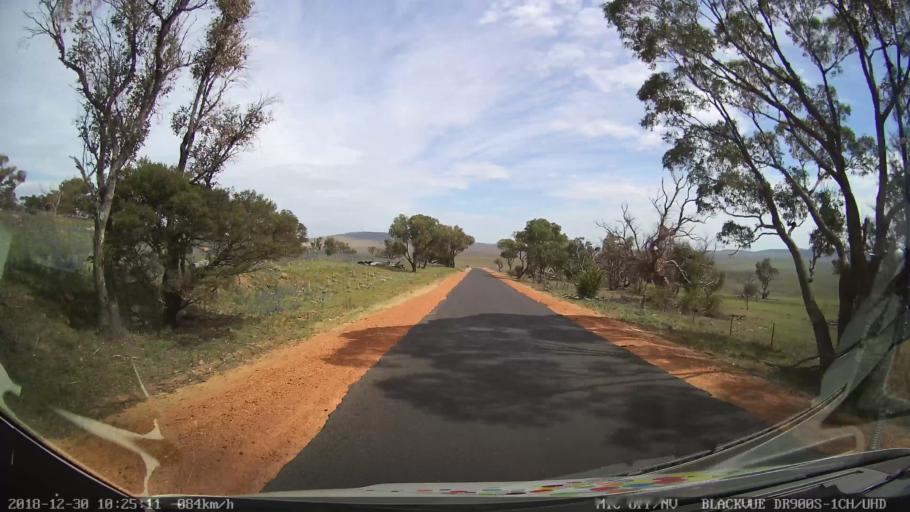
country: AU
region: New South Wales
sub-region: Snowy River
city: Berridale
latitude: -36.5273
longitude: 148.9608
